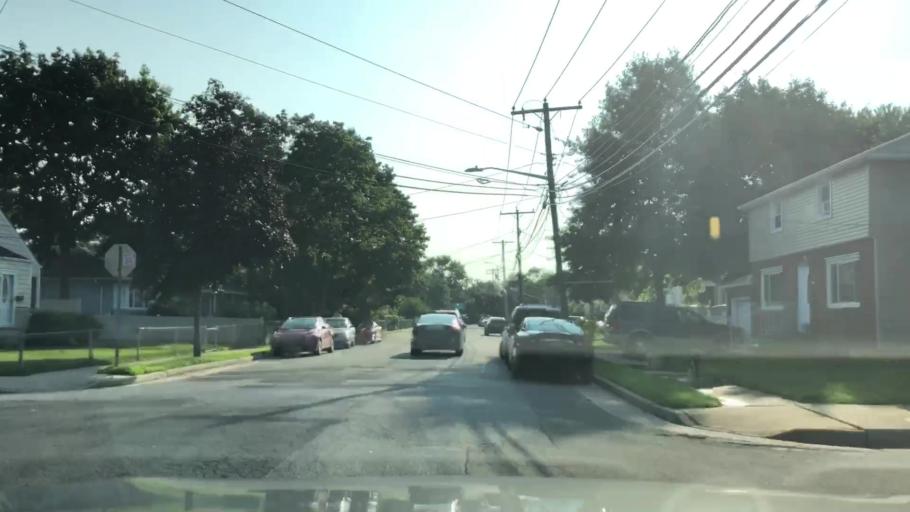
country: US
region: New York
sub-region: Nassau County
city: South Hempstead
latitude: 40.6927
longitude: -73.6113
